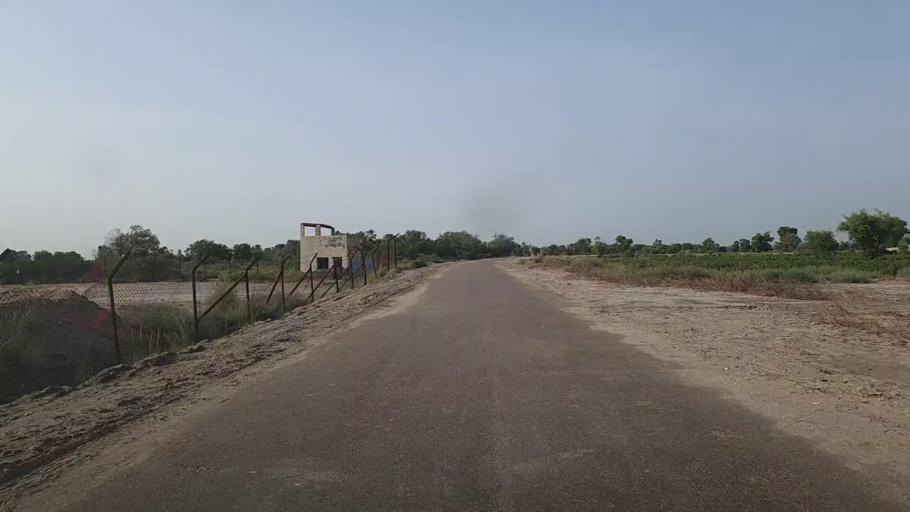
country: PK
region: Sindh
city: Ubauro
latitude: 28.0978
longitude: 69.8456
